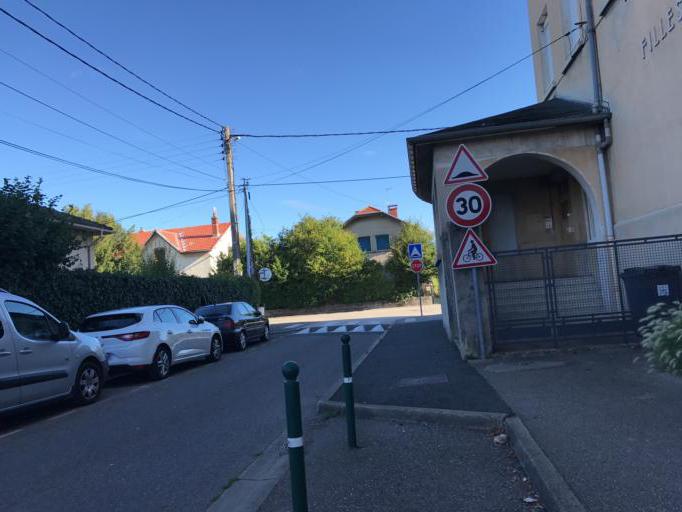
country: FR
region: Rhone-Alpes
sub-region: Departement de l'Ain
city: Amberieu-en-Bugey
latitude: 45.9574
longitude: 5.3436
